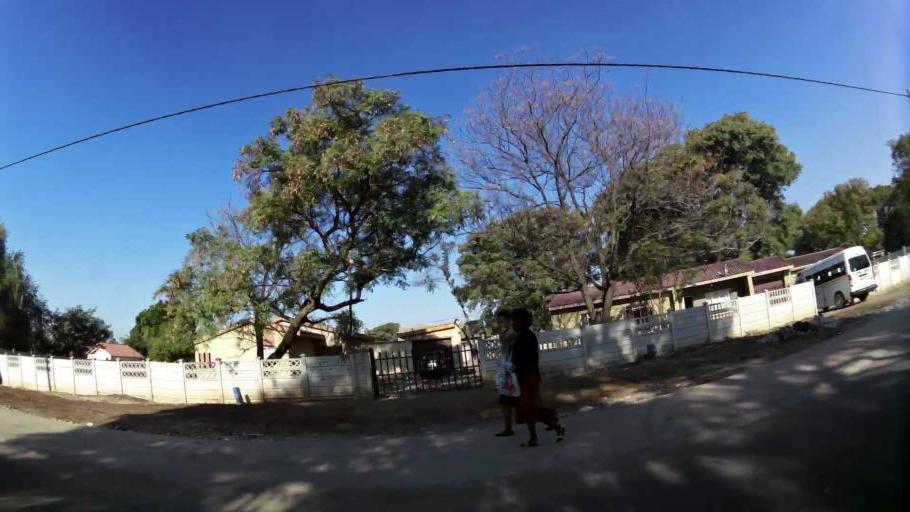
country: ZA
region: North-West
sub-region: Bojanala Platinum District Municipality
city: Rustenburg
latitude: -25.6552
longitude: 27.2298
